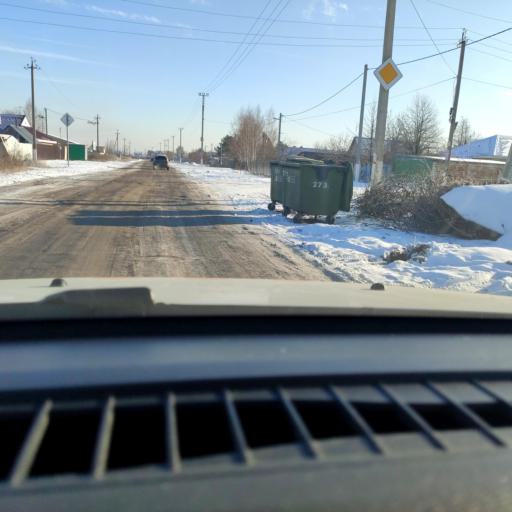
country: RU
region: Samara
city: Podstepki
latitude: 53.5194
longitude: 49.1348
